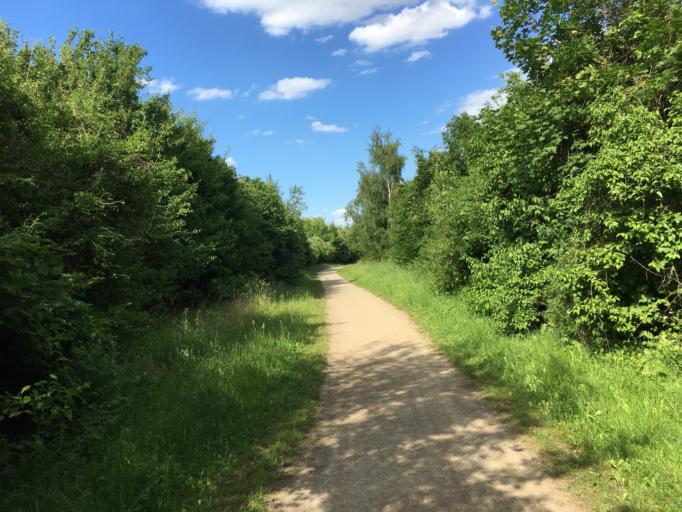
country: DE
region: North Rhine-Westphalia
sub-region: Regierungsbezirk Koln
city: Dueren
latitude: 50.7803
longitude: 6.4743
